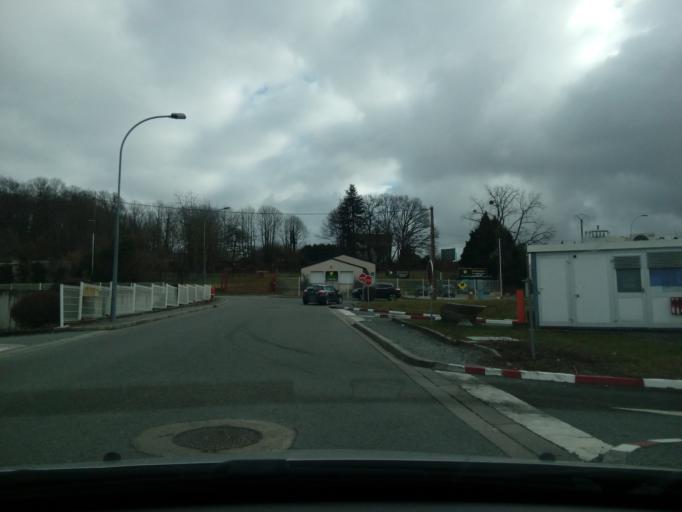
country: FR
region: Limousin
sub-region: Departement de la Creuse
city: Gueret
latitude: 46.1678
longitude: 1.8881
